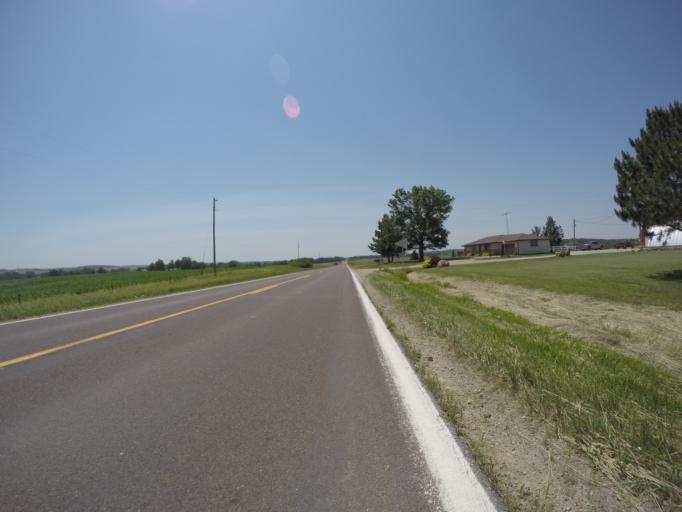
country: US
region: Nebraska
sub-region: Pawnee County
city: Pawnee City
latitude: 40.0167
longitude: -96.0484
